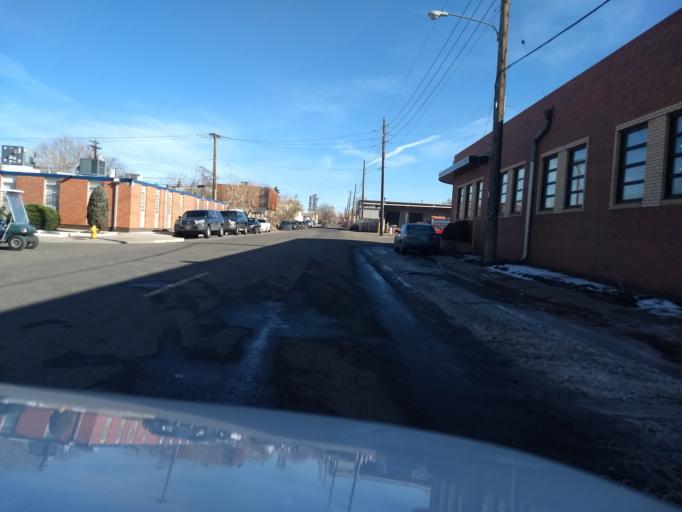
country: US
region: Colorado
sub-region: Denver County
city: Denver
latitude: 39.7148
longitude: -104.9954
